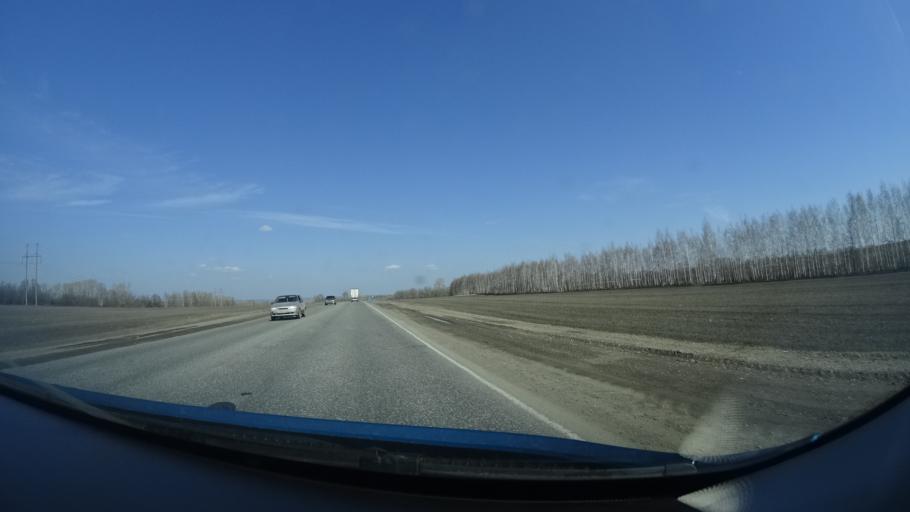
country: RU
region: Bashkortostan
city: Subkhankulovo
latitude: 54.5068
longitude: 53.9497
